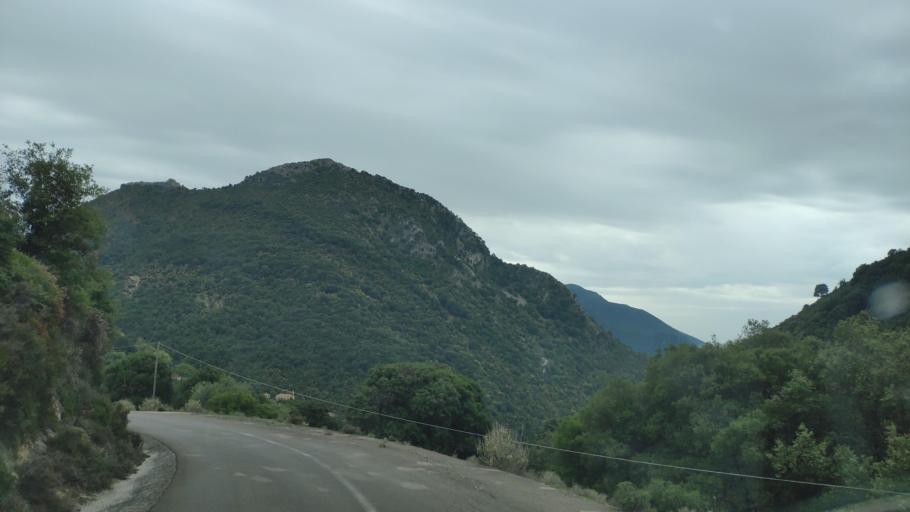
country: GR
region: Epirus
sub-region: Nomos Prevezis
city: Kanalaki
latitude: 39.3489
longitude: 20.6486
